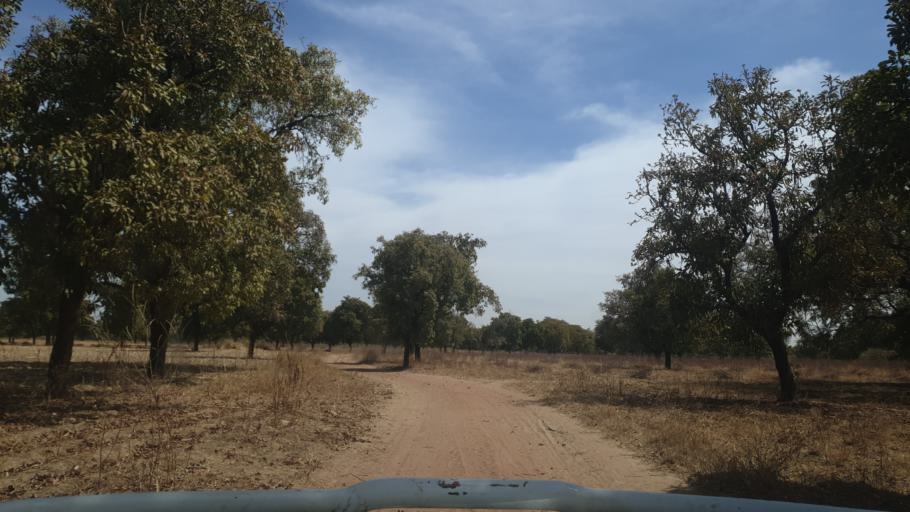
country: ML
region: Sikasso
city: Yorosso
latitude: 12.2880
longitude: -4.6736
